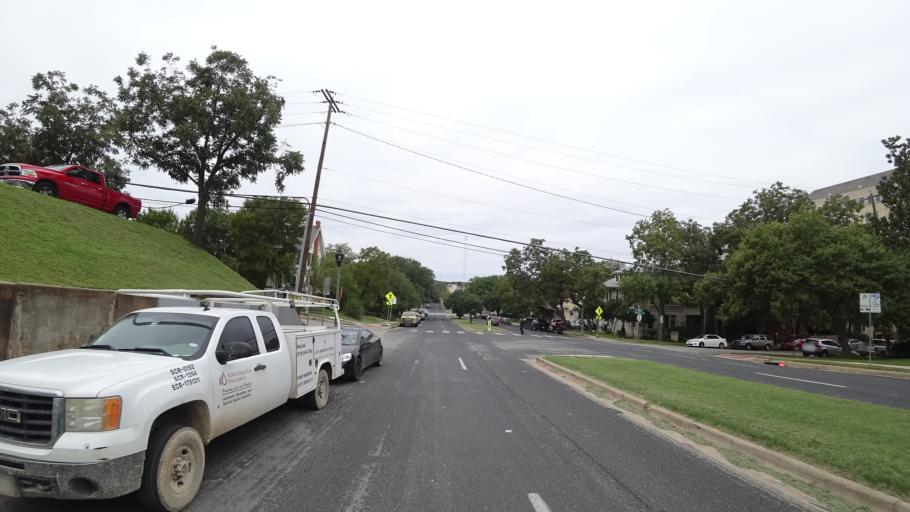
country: US
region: Texas
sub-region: Travis County
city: Austin
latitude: 30.2750
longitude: -97.7450
